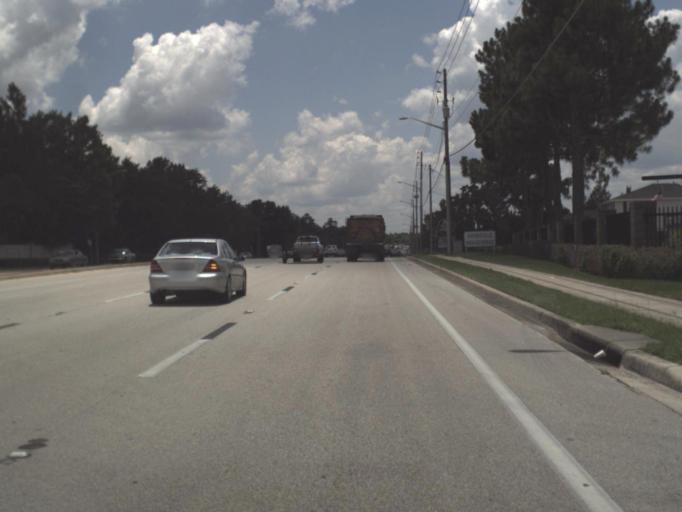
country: US
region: Florida
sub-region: Alachua County
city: Gainesville
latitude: 29.6134
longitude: -82.3721
